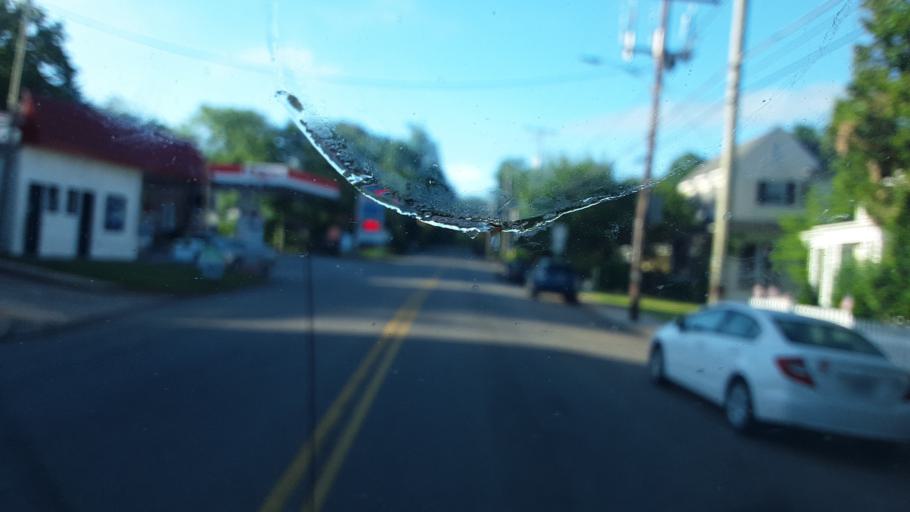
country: US
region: Virginia
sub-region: Pittsylvania County
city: Chatham
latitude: 36.8234
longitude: -79.3974
